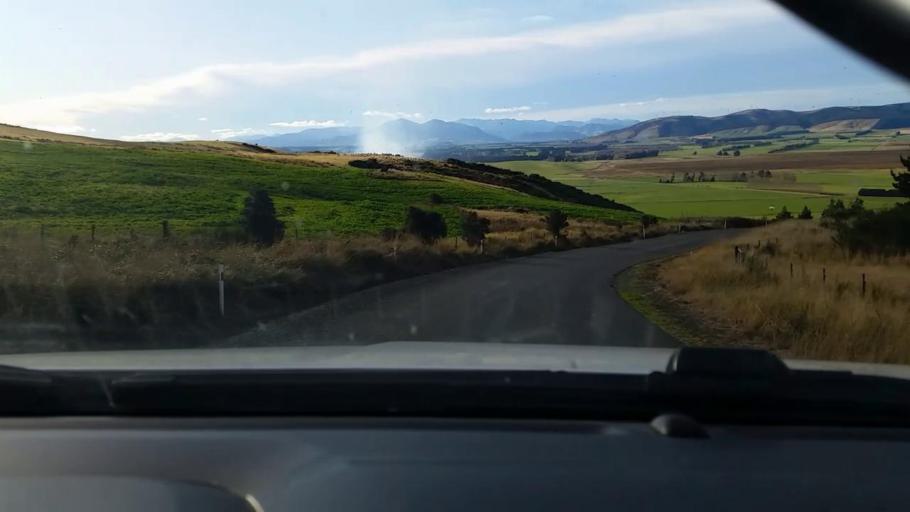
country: NZ
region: Southland
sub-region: Southland District
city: Winton
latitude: -45.8196
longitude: 168.1740
